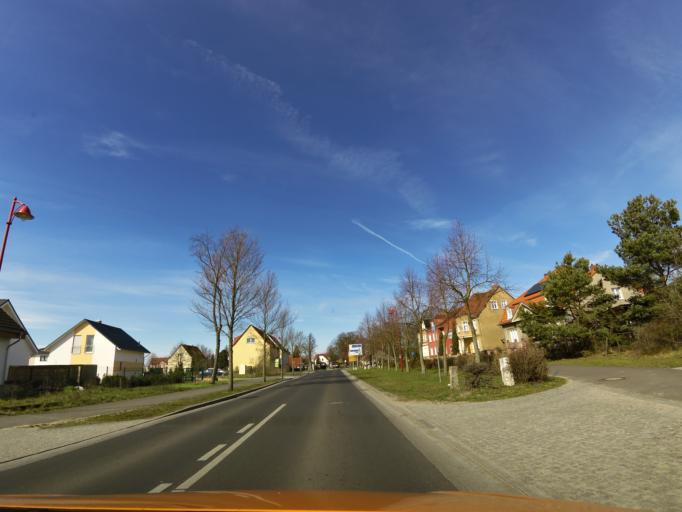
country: DE
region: Brandenburg
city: Beelitz
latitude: 52.2376
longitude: 12.9662
